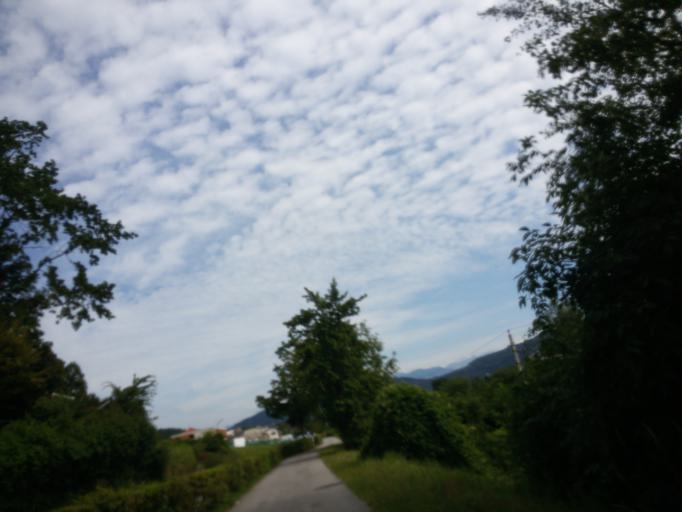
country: AT
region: Carinthia
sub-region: Politischer Bezirk Klagenfurt Land
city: Maria Worth
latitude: 46.6273
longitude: 14.1740
